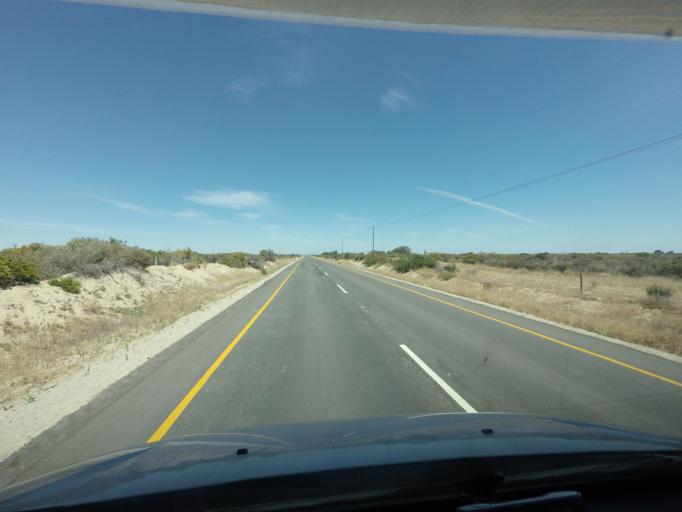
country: ZA
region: Western Cape
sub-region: West Coast District Municipality
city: Vredenburg
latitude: -32.7958
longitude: 18.2540
